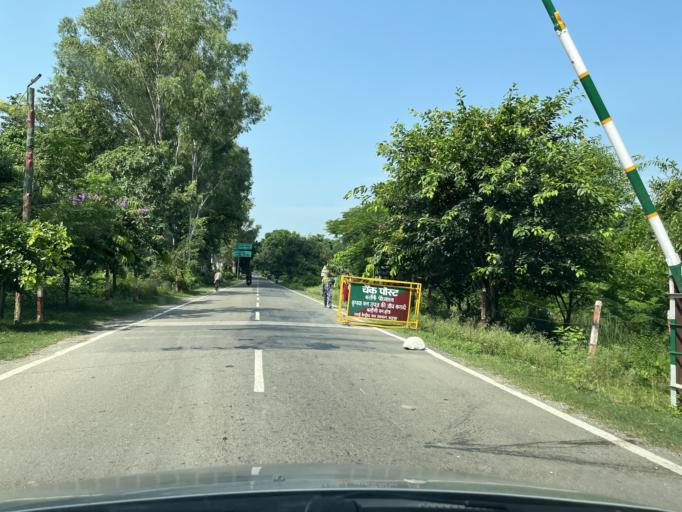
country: IN
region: Uttarakhand
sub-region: Naini Tal
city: Kaladhungi
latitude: 29.2197
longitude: 79.2329
